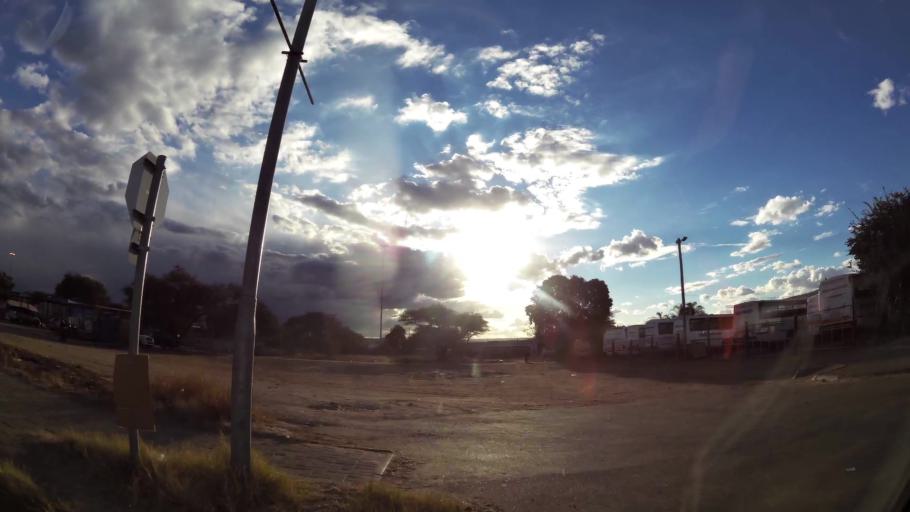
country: ZA
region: Limpopo
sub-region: Capricorn District Municipality
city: Polokwane
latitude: -23.9028
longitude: 29.4312
